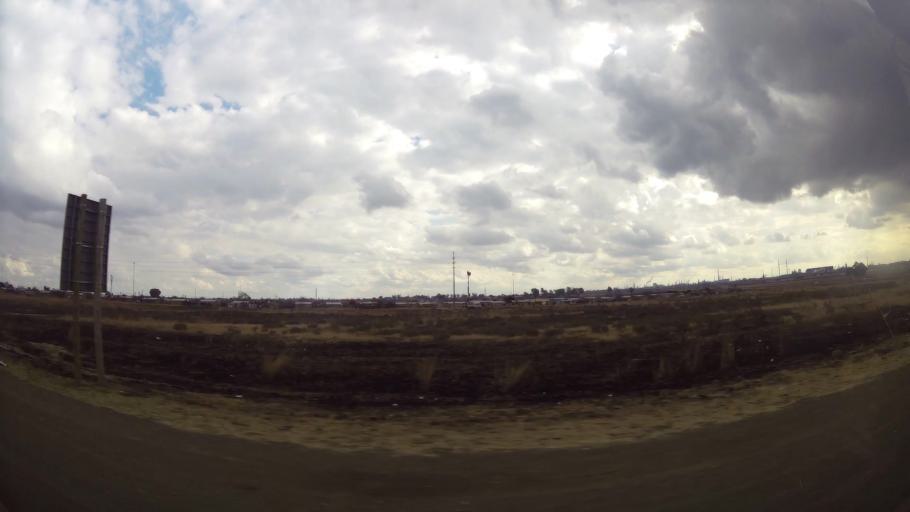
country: ZA
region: Orange Free State
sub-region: Fezile Dabi District Municipality
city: Sasolburg
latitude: -26.8480
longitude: 27.8891
